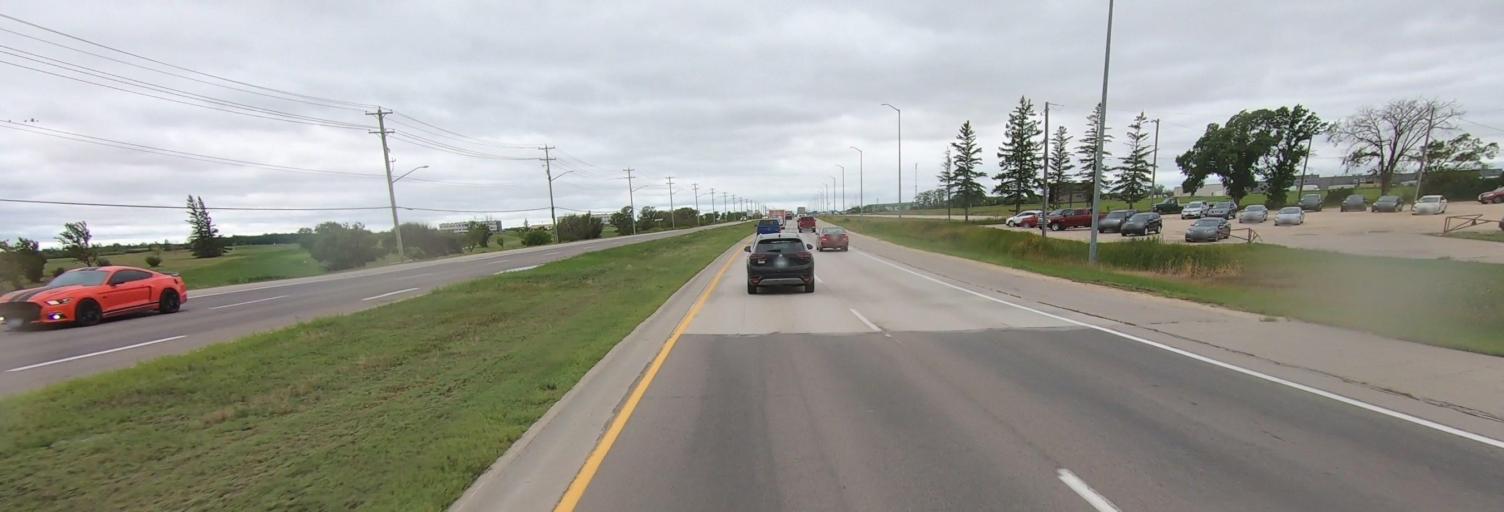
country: CA
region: Manitoba
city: Headingley
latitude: 49.8763
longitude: -97.3630
